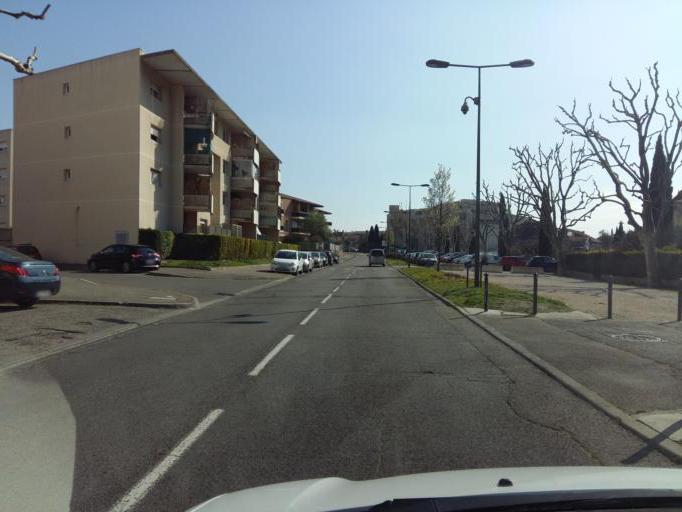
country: FR
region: Provence-Alpes-Cote d'Azur
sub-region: Departement du Vaucluse
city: Cavaillon
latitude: 43.8410
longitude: 5.0397
